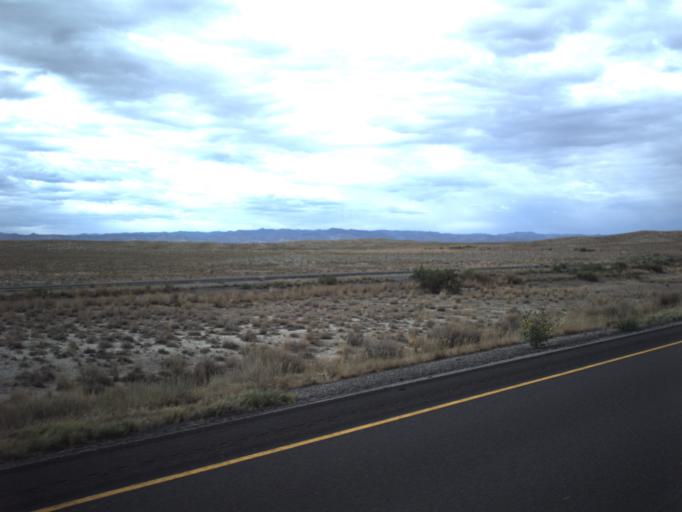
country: US
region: Colorado
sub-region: Mesa County
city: Loma
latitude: 39.0989
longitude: -109.2027
